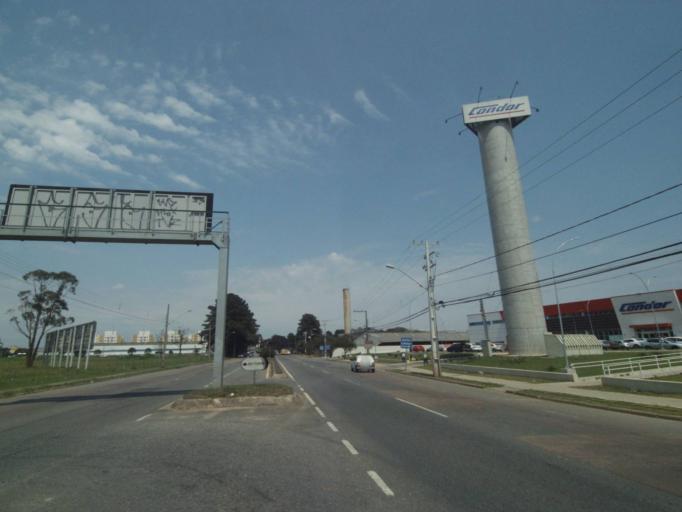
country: BR
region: Parana
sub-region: Curitiba
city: Curitiba
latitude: -25.4929
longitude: -49.3236
